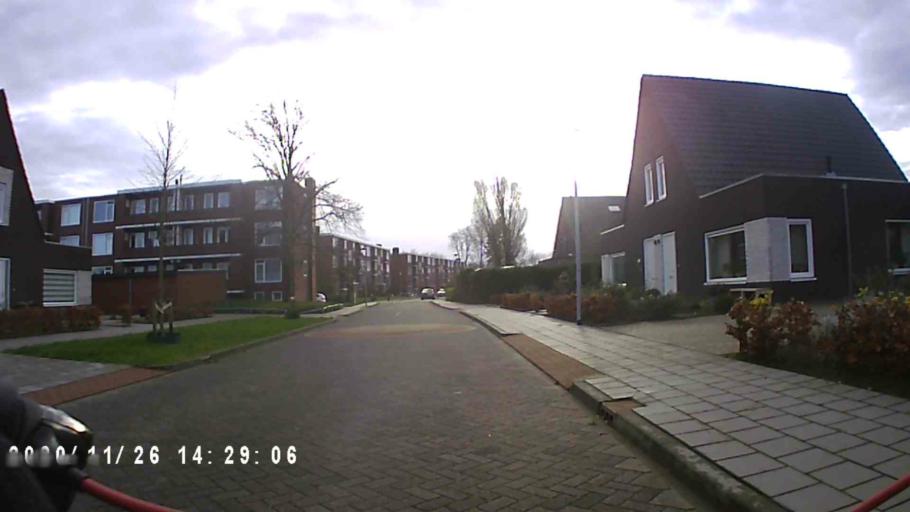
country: NL
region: Groningen
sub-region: Gemeente Appingedam
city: Appingedam
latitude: 53.3162
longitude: 6.8679
